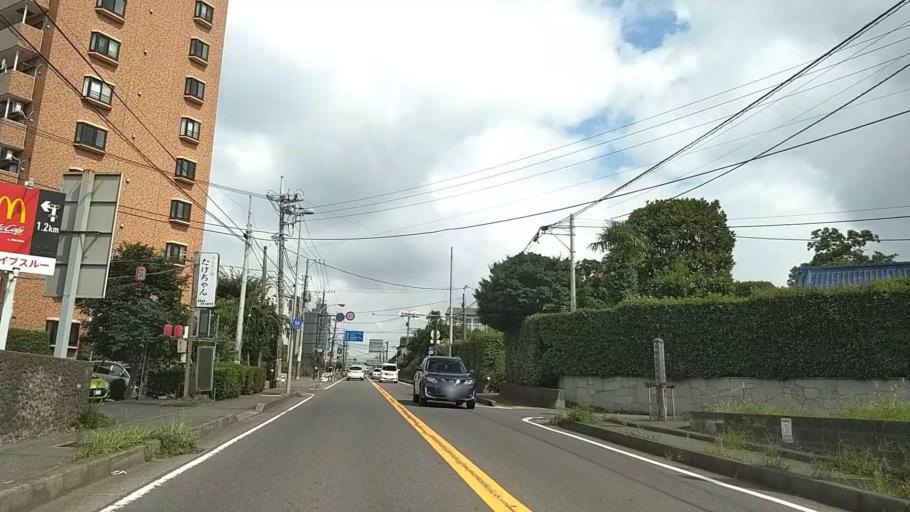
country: JP
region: Kanagawa
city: Minami-rinkan
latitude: 35.5022
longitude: 139.4661
